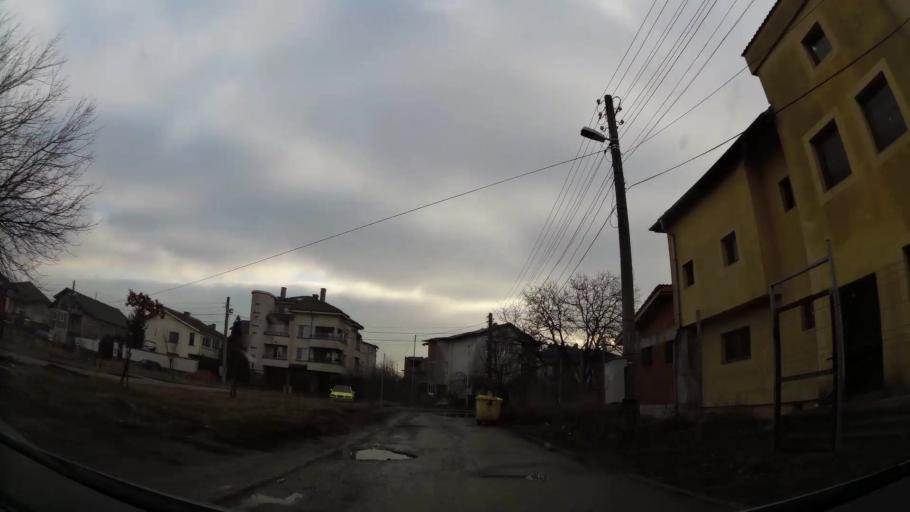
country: BG
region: Sofia-Capital
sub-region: Stolichna Obshtina
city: Sofia
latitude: 42.7455
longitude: 23.3506
